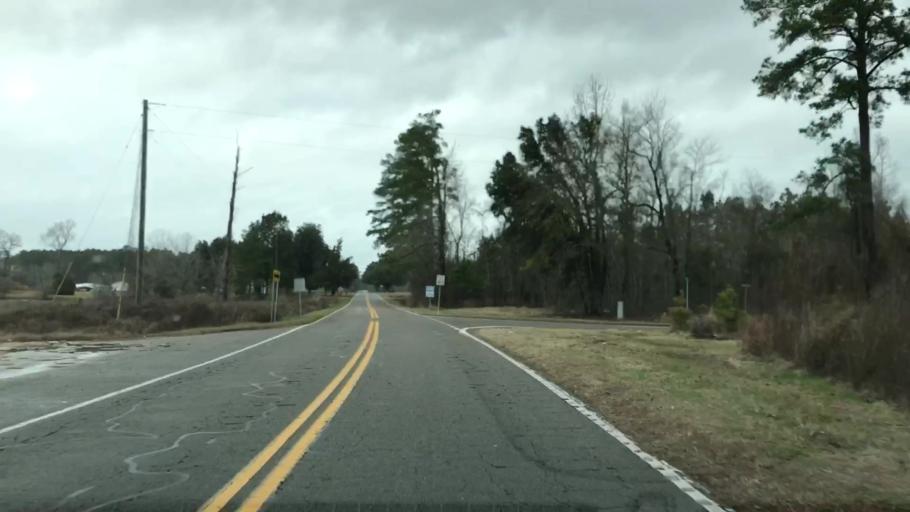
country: US
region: South Carolina
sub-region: Florence County
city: Johnsonville
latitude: 33.6611
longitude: -79.3051
